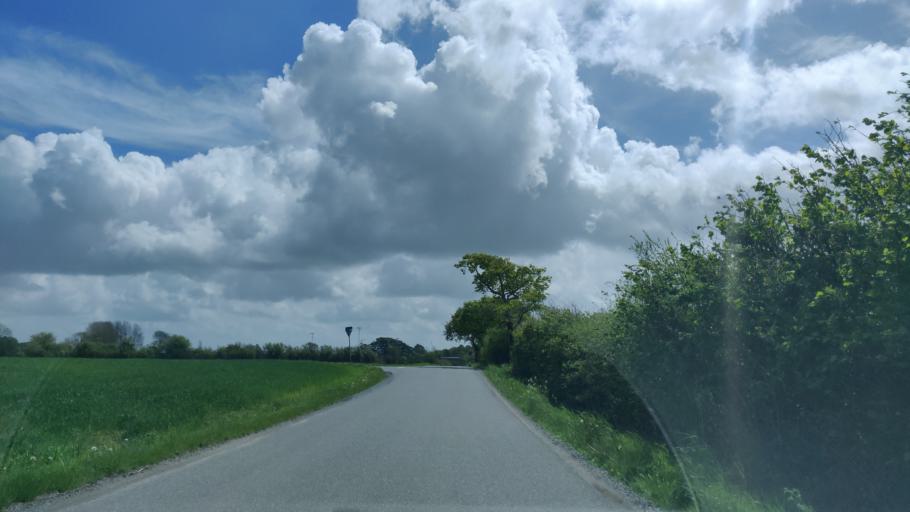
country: DK
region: South Denmark
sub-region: Vejle Kommune
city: Vejle
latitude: 55.6522
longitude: 9.5374
